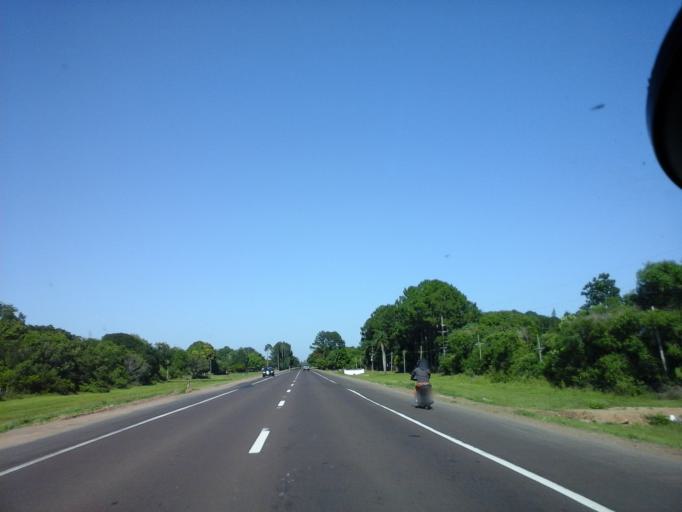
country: AR
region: Corrientes
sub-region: Departamento de San Cosme
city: San Cosme
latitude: -27.3684
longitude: -58.4122
